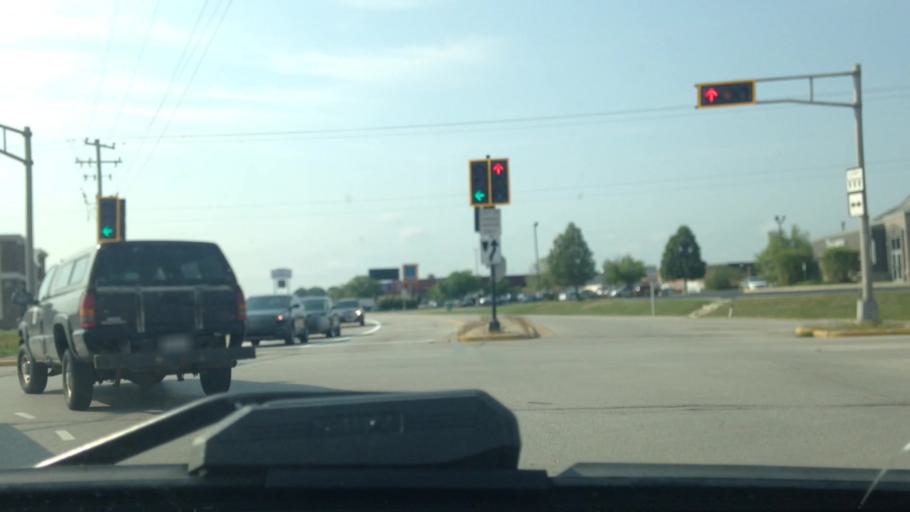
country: US
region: Wisconsin
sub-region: Fond du Lac County
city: North Fond du Lac
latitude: 43.7847
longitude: -88.4860
